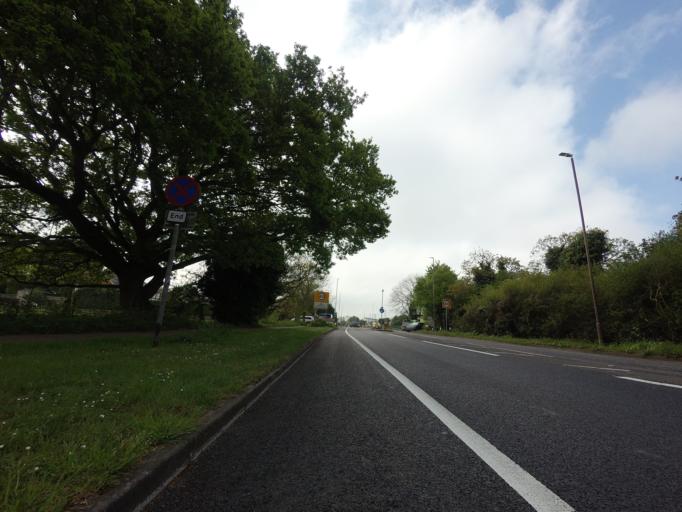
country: GB
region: England
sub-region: Kent
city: Eynsford
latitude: 51.3540
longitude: 0.2526
